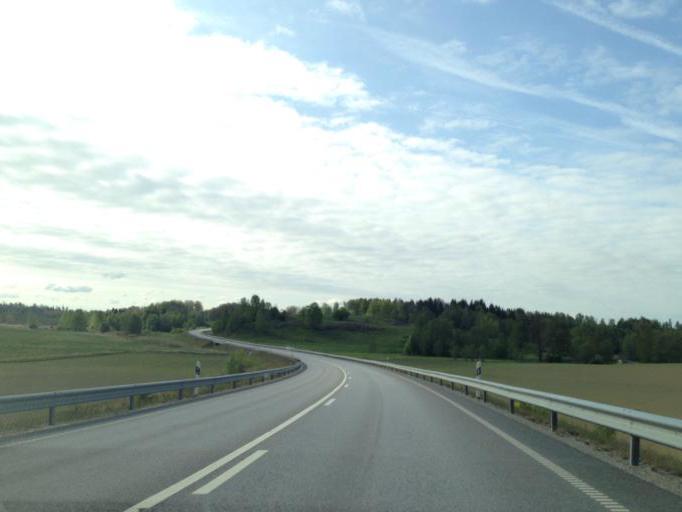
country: SE
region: Soedermanland
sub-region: Flens Kommun
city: Malmkoping
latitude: 59.1358
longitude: 16.7132
